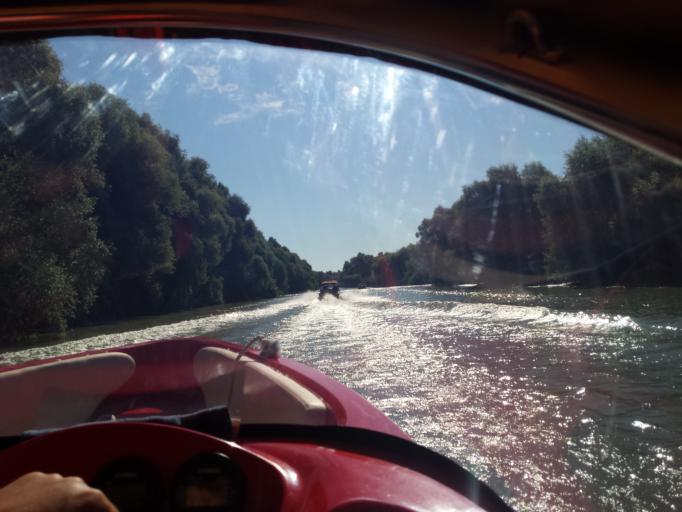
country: RO
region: Tulcea
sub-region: Comuna Pardina
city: Pardina
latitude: 45.2553
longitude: 28.9685
